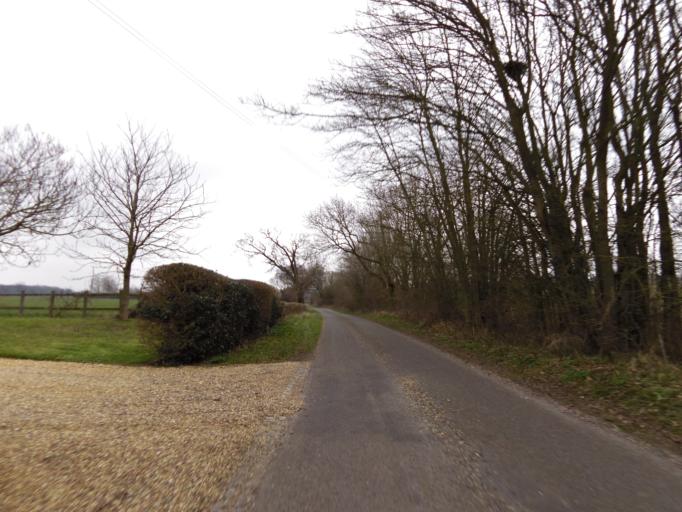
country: GB
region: England
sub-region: Suffolk
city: Framlingham
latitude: 52.1912
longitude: 1.3314
